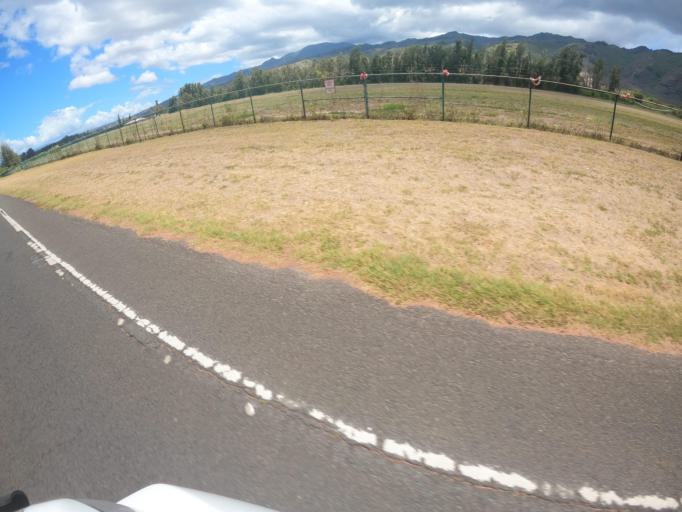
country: US
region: Hawaii
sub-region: Honolulu County
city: Mokuleia
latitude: 21.5812
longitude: -158.1885
